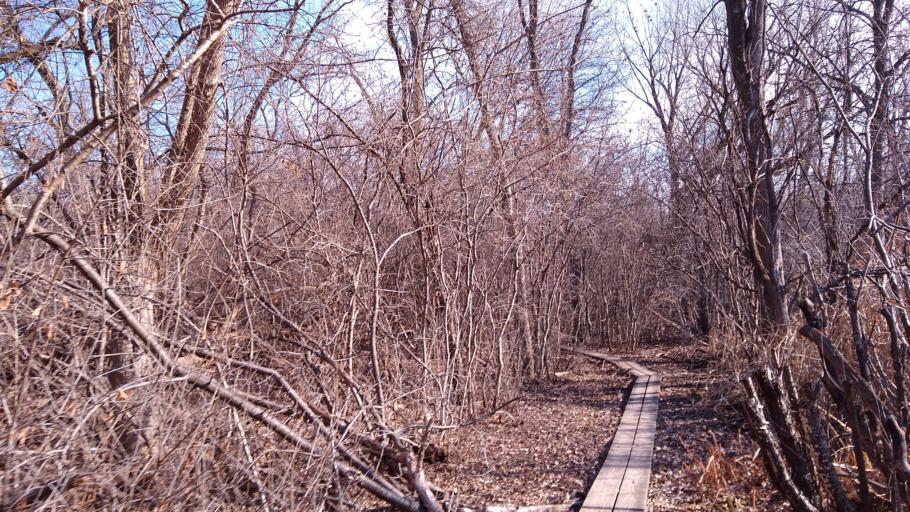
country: US
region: Wisconsin
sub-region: Dane County
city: Madison
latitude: 43.0560
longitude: -89.4055
